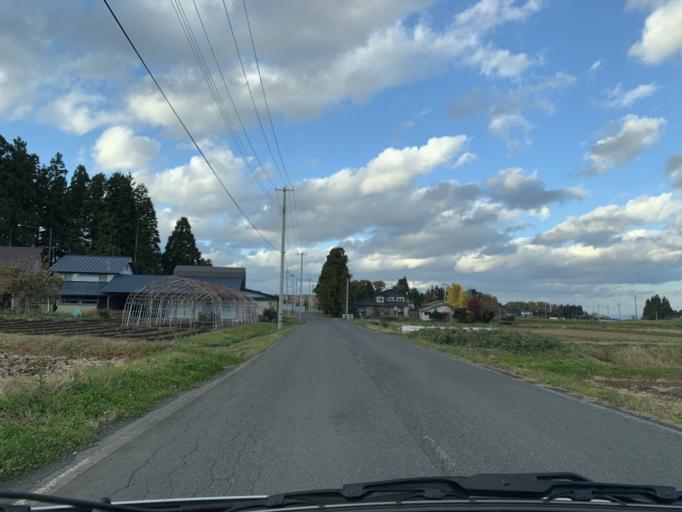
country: JP
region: Iwate
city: Mizusawa
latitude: 39.1105
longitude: 141.0238
